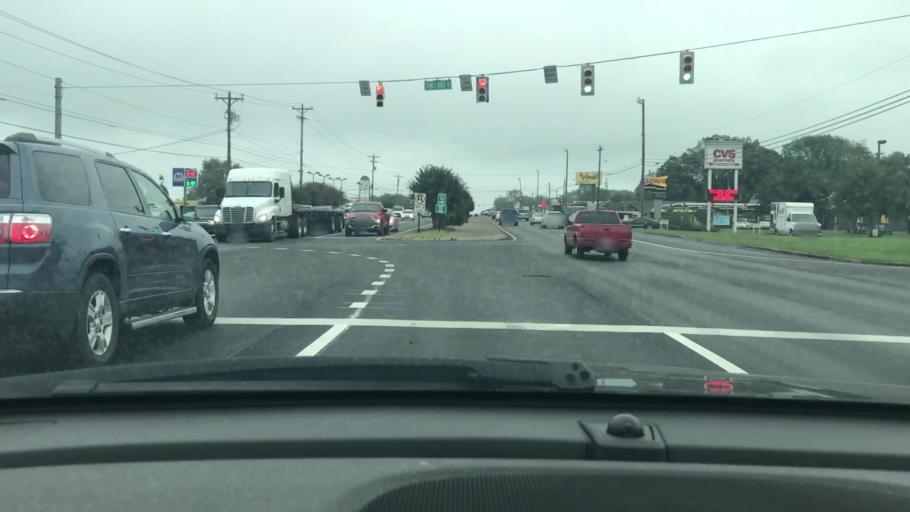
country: US
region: Tennessee
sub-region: Rutherford County
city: La Vergne
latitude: 36.0192
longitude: -86.5729
